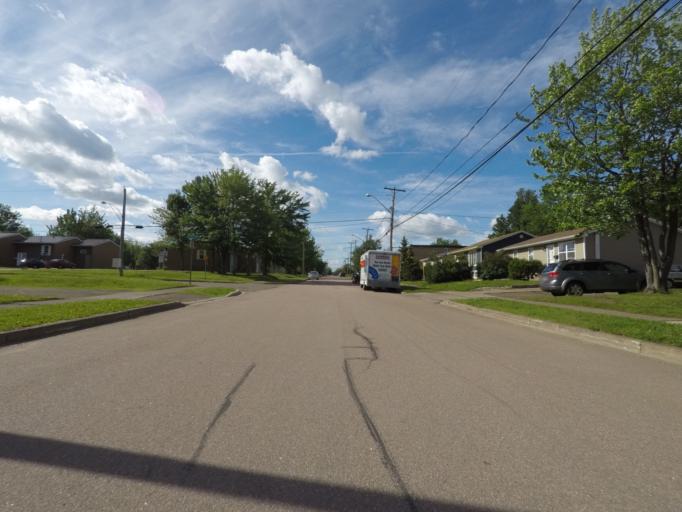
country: CA
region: New Brunswick
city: Moncton
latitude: 46.0985
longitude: -64.8225
